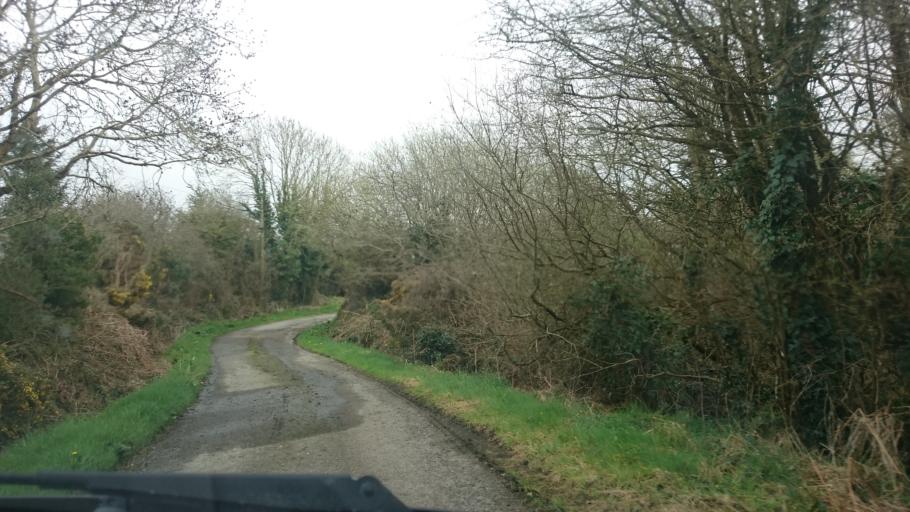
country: IE
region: Munster
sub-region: Waterford
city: Waterford
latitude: 52.2265
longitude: -7.0354
